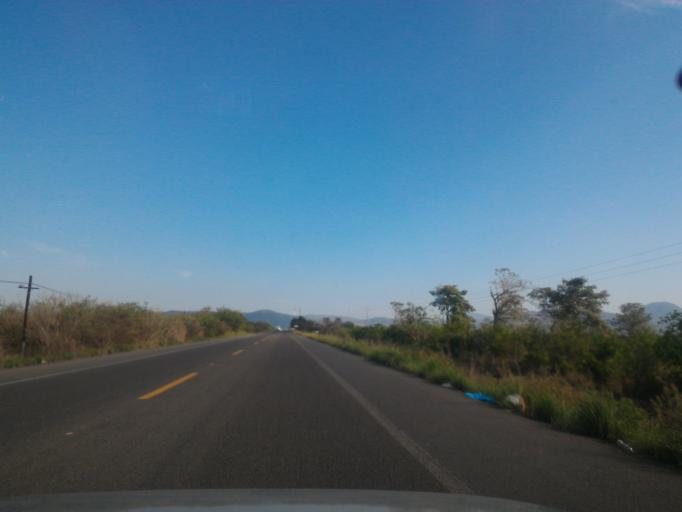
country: MX
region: Michoacan
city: Coahuayana Viejo
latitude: 18.7385
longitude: -103.7238
